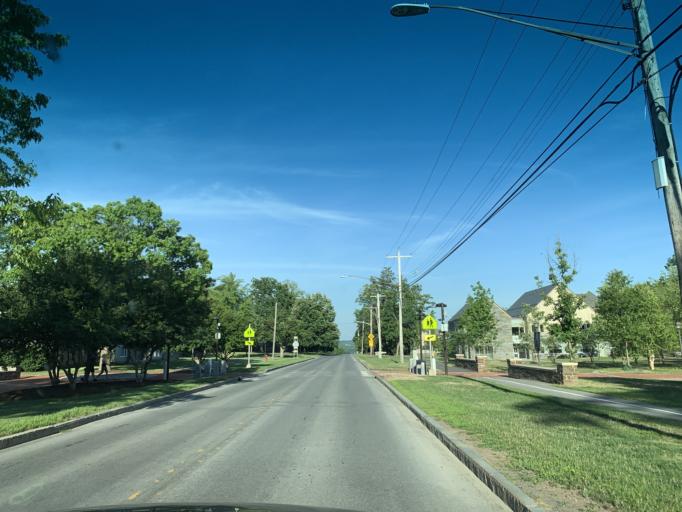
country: US
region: New York
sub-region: Oneida County
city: Clinton
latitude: 43.0506
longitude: -75.4081
